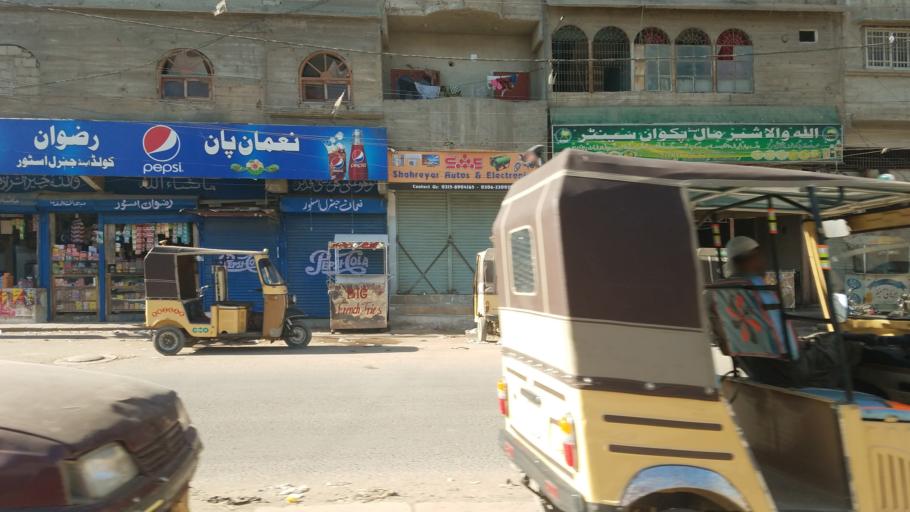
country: PK
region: Sindh
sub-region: Karachi District
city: Karachi
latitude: 24.9205
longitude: 67.0514
